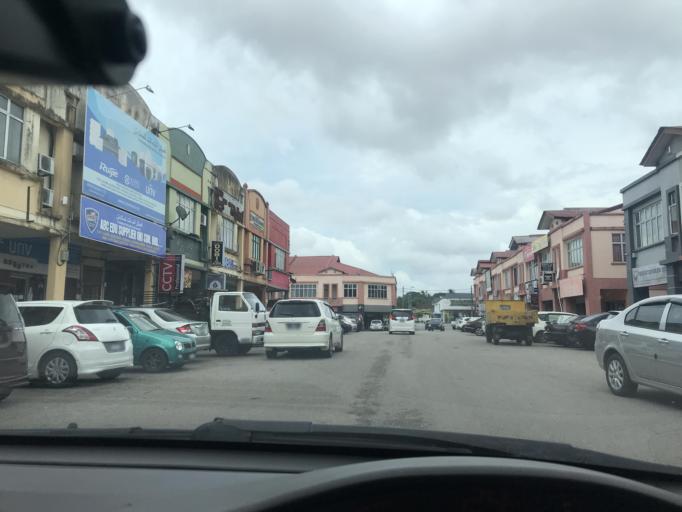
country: MY
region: Kelantan
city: Kota Bharu
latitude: 6.1201
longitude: 102.2170
